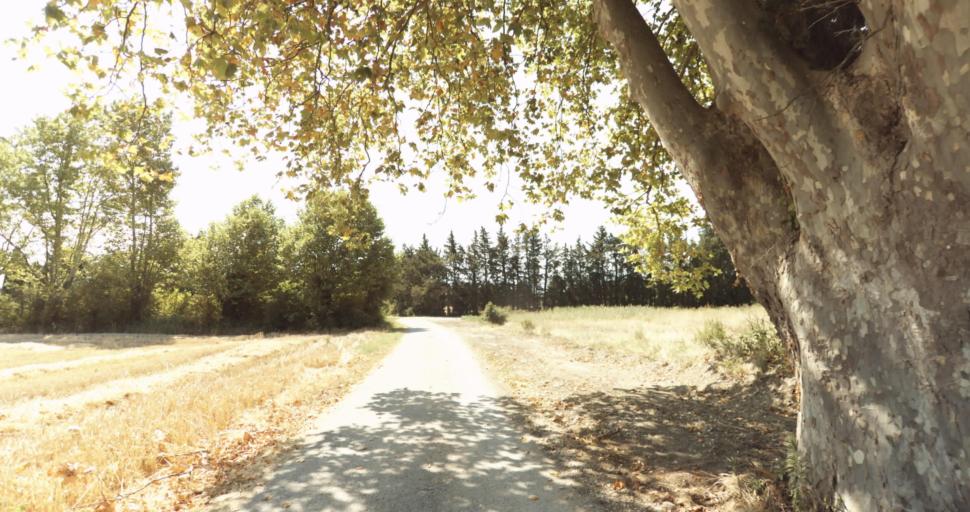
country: FR
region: Provence-Alpes-Cote d'Azur
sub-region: Departement du Vaucluse
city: Monteux
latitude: 44.0244
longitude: 4.9883
